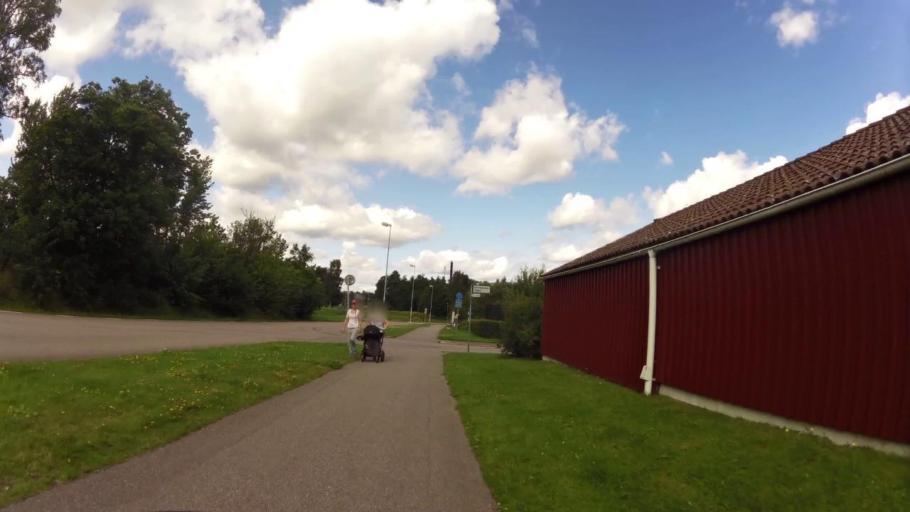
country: SE
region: OEstergoetland
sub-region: Linkopings Kommun
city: Ljungsbro
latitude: 58.4959
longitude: 15.5035
